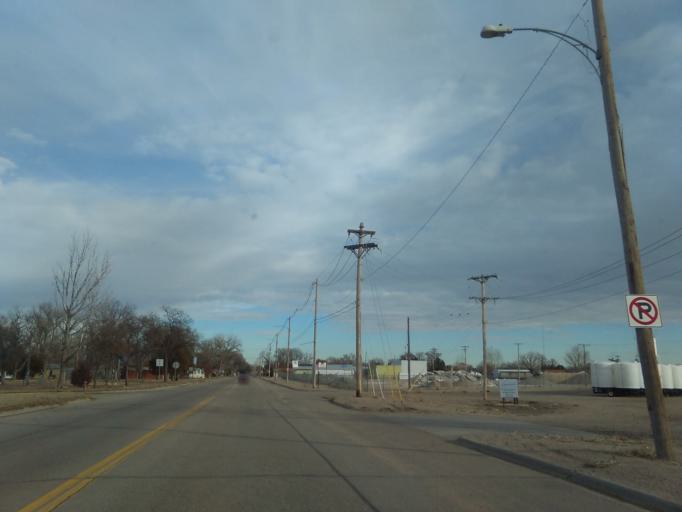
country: US
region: Nebraska
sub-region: Morrill County
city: Bridgeport
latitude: 41.6703
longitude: -103.1077
